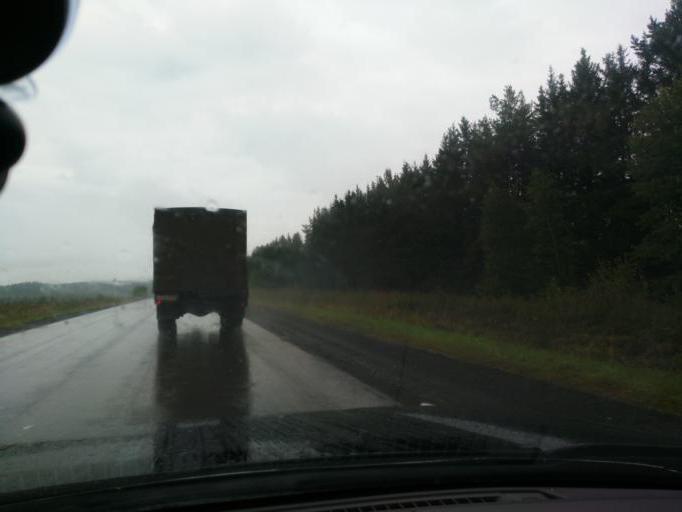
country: RU
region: Perm
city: Yugo-Kamskiy
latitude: 57.4714
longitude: 55.6767
